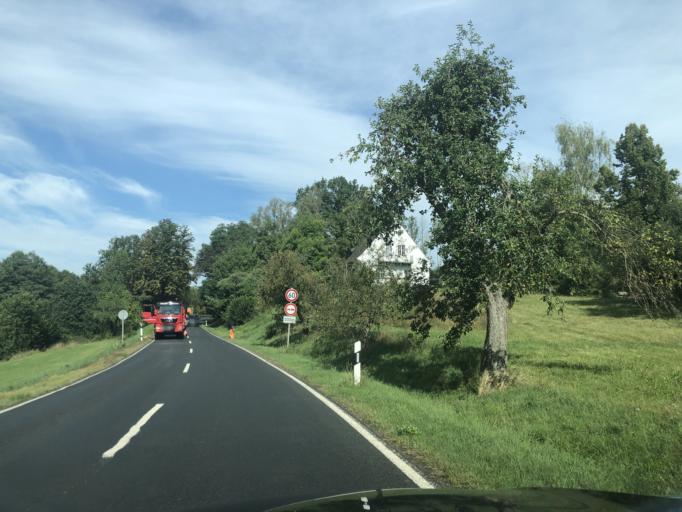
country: DE
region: Bavaria
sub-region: Upper Palatinate
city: Pressath
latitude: 49.7759
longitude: 11.9289
